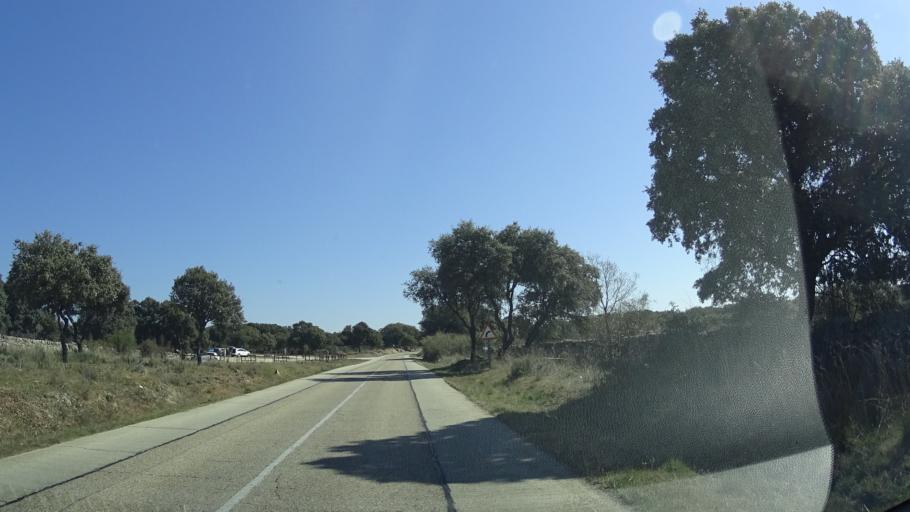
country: ES
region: Madrid
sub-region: Provincia de Madrid
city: Hoyo de Manzanares
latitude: 40.6444
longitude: -3.8418
